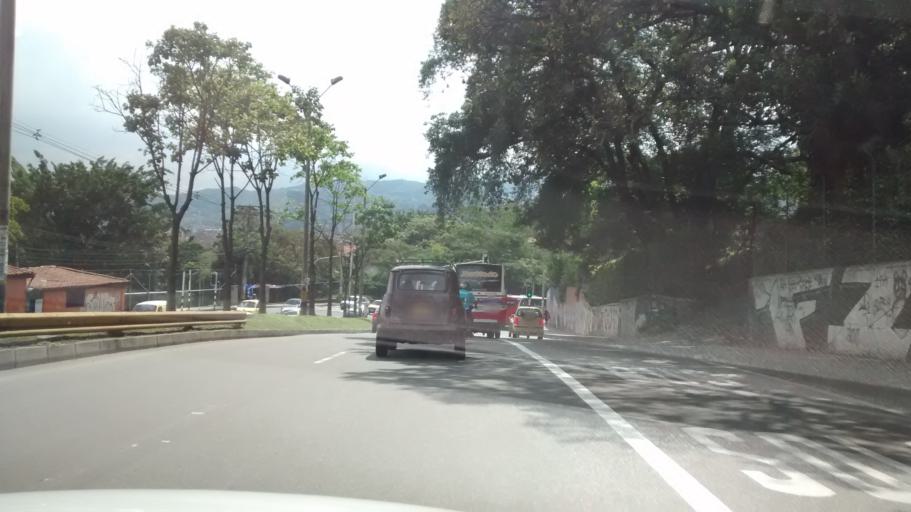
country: CO
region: Antioquia
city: Medellin
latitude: 6.2768
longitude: -75.5899
